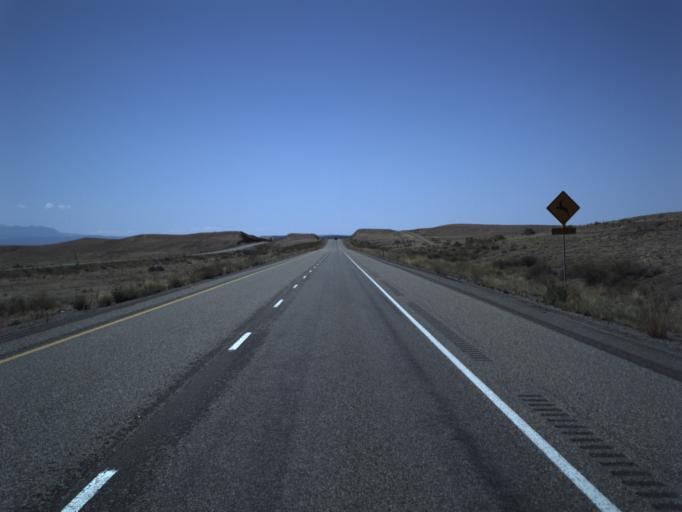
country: US
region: Colorado
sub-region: Mesa County
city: Loma
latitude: 39.1516
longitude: -109.1483
